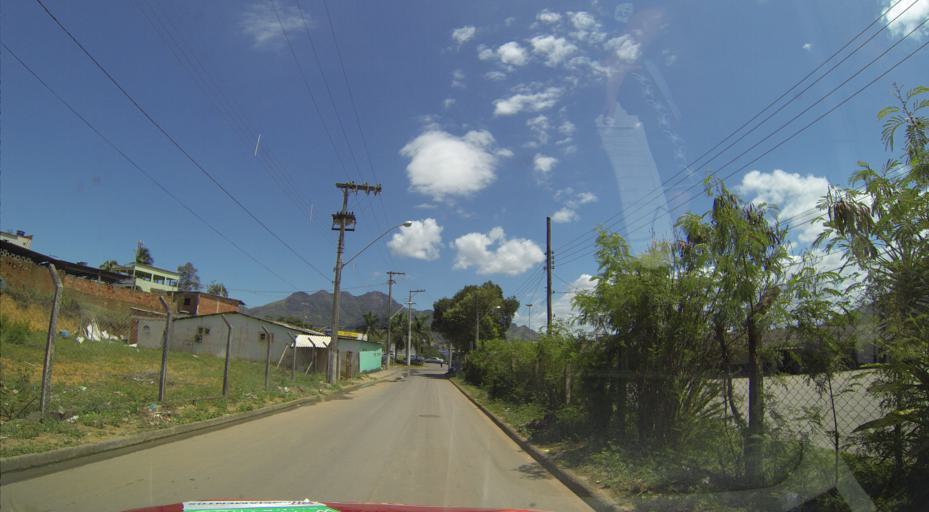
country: BR
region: Espirito Santo
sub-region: Serra
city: Serra
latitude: -20.1165
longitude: -40.3145
